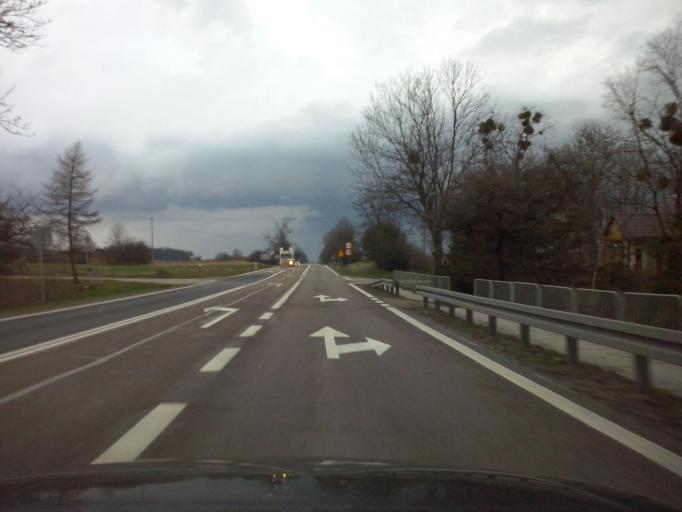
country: PL
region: Lublin Voivodeship
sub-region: Powiat chelmski
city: Rejowiec Fabryczny
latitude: 51.1742
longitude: 23.2676
